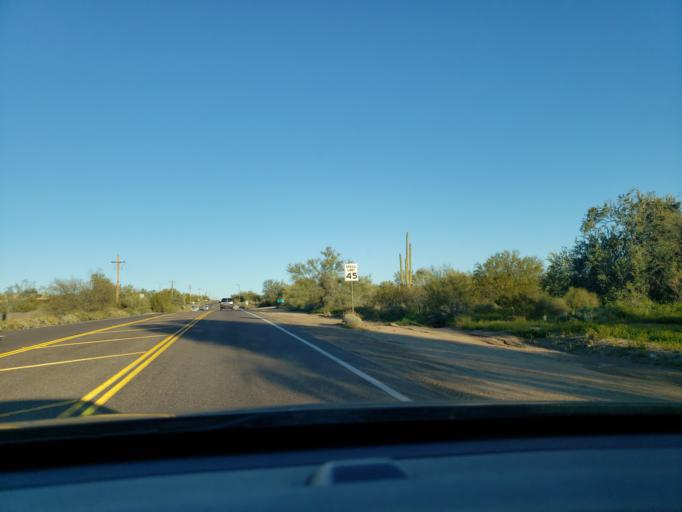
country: US
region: Arizona
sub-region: Maricopa County
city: Cave Creek
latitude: 33.7991
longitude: -111.9509
